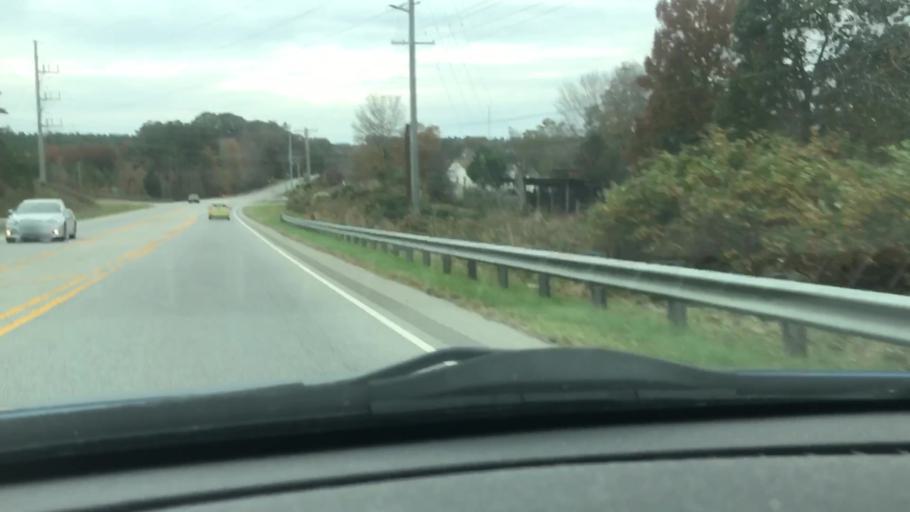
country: US
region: North Carolina
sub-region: Davidson County
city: Thomasville
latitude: 35.7528
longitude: -80.0350
